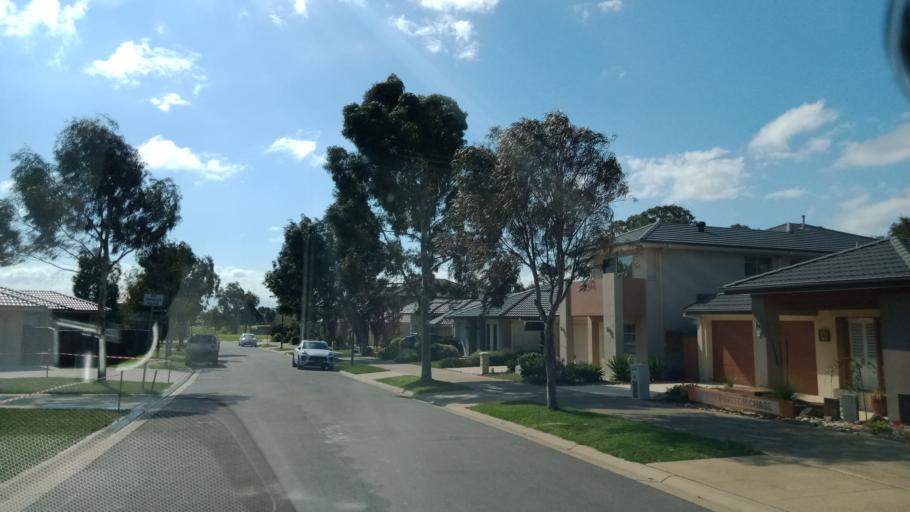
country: AU
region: Victoria
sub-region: Frankston
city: Sandhurst
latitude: -38.0832
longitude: 145.2114
